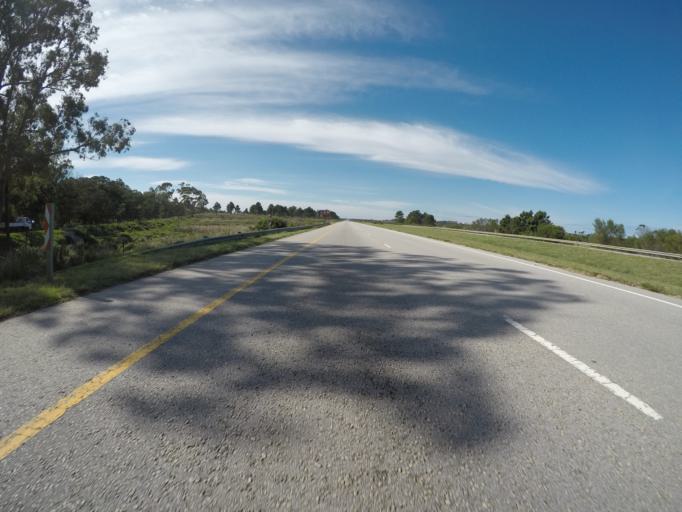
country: ZA
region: Eastern Cape
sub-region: Nelson Mandela Bay Metropolitan Municipality
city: Uitenhage
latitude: -33.9271
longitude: 25.3287
